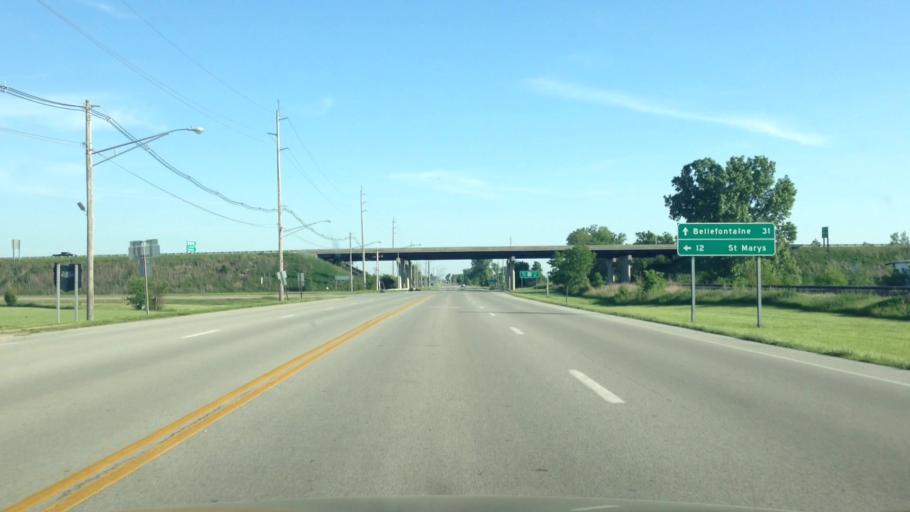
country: US
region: Ohio
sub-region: Auglaize County
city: Wapakoneta
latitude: 40.5577
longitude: -84.1938
